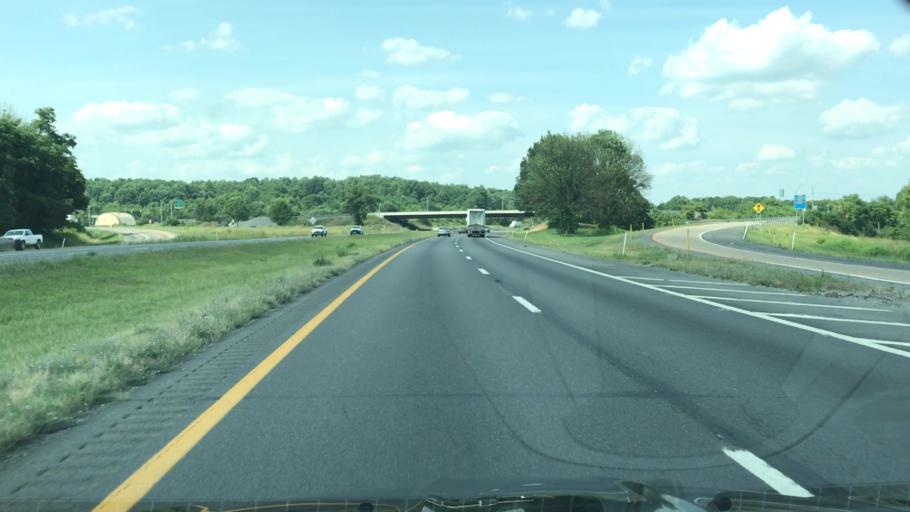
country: US
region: West Virginia
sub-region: Berkeley County
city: Inwood
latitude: 39.4040
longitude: -78.0259
